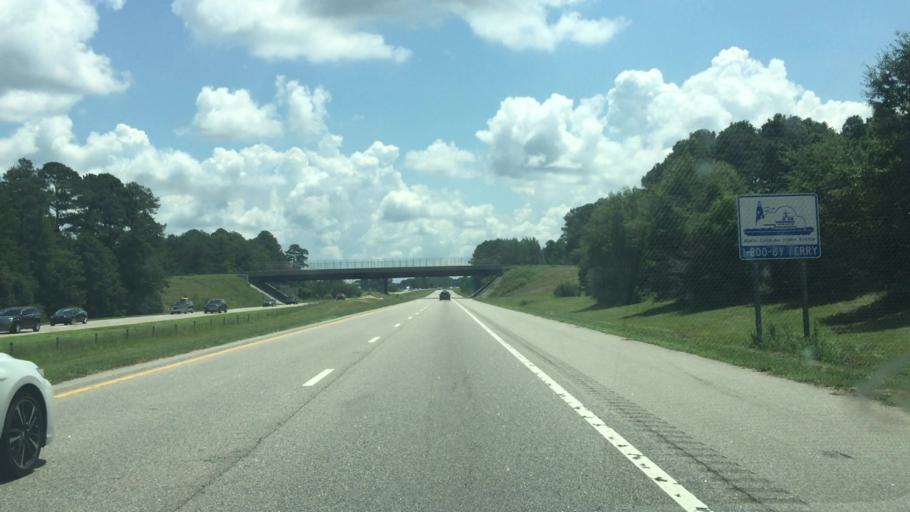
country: US
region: North Carolina
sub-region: Robeson County
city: Lumberton
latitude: 34.5910
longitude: -79.0709
